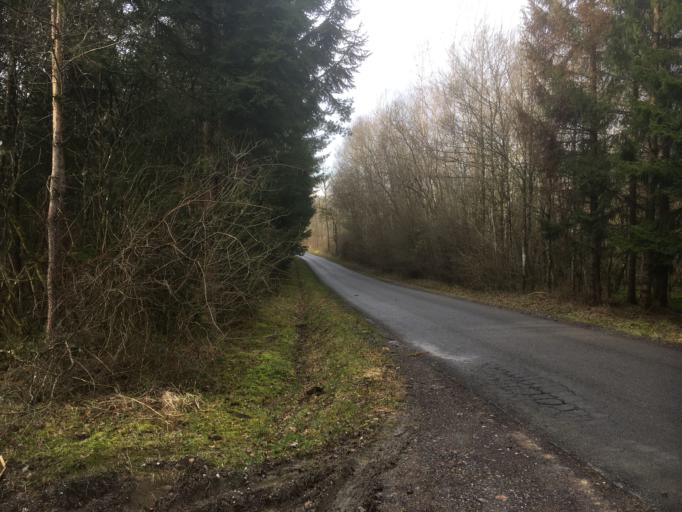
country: BE
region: Wallonia
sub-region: Province du Luxembourg
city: Durbuy
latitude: 50.3190
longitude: 5.4978
